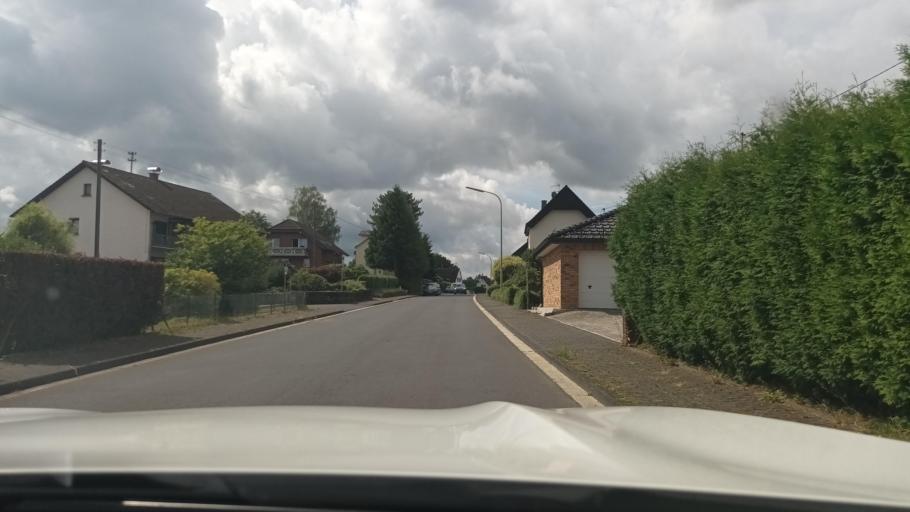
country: DE
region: North Rhine-Westphalia
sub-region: Regierungsbezirk Koln
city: Eitorf
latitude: 50.7541
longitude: 7.4314
